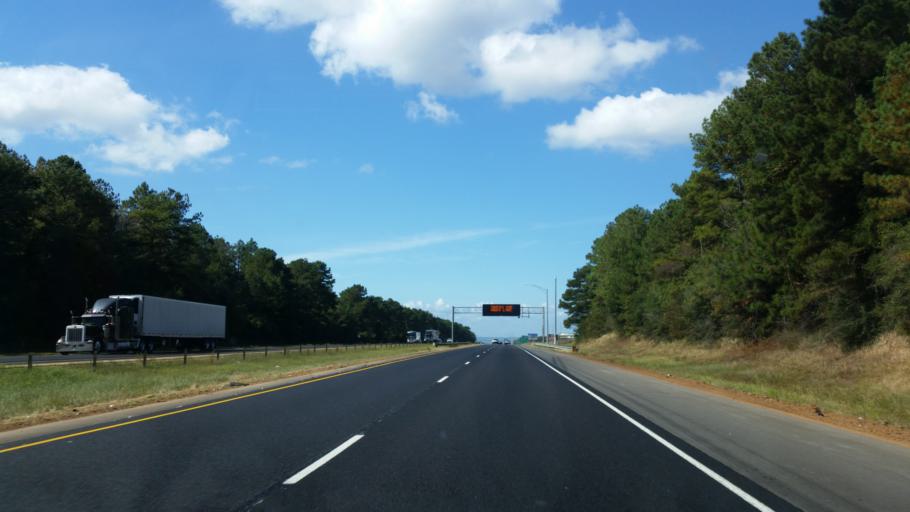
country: US
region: Alabama
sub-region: Baldwin County
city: Spanish Fort
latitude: 30.6585
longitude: -87.8920
